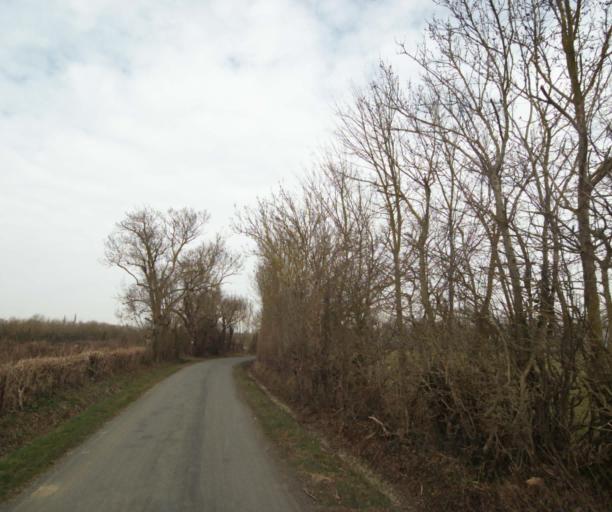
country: FR
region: Poitou-Charentes
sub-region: Departement des Deux-Sevres
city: Niort
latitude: 46.3003
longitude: -0.4679
